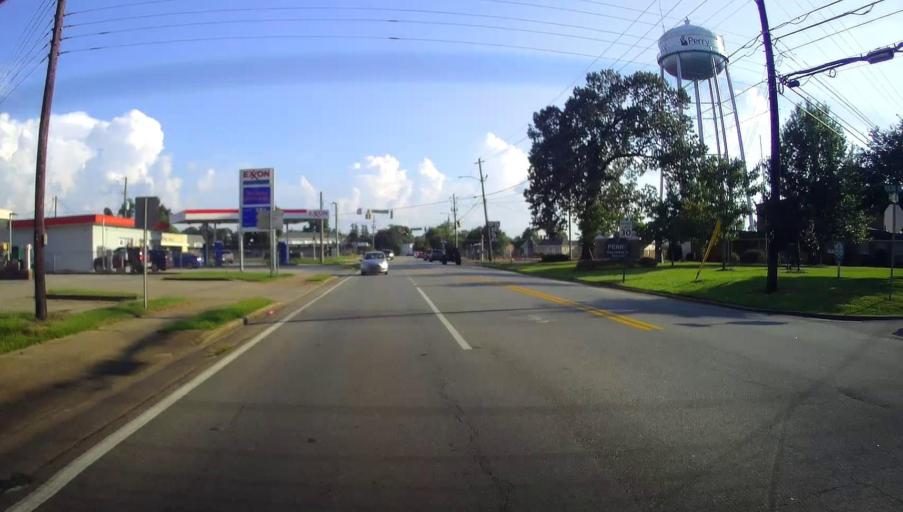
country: US
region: Georgia
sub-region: Houston County
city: Perry
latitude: 32.4611
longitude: -83.7309
